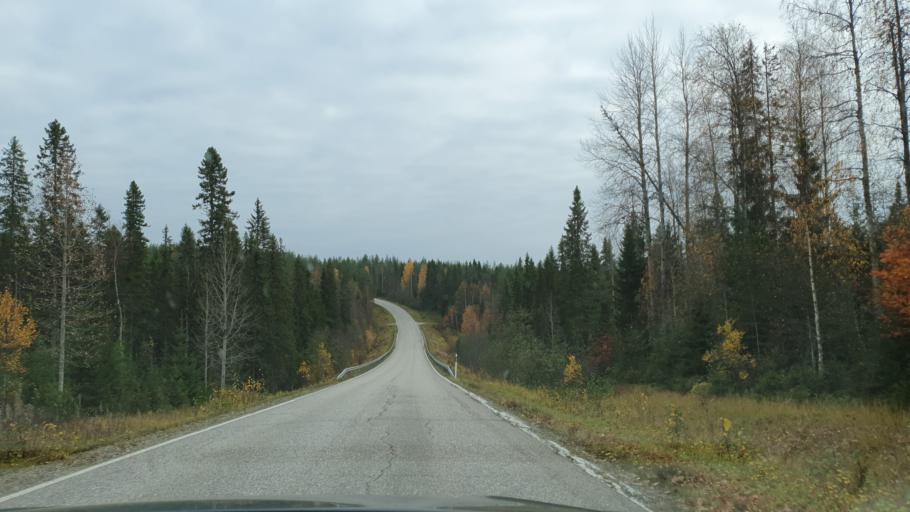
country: FI
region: Kainuu
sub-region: Kajaani
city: Ristijaervi
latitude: 64.4738
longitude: 28.2879
